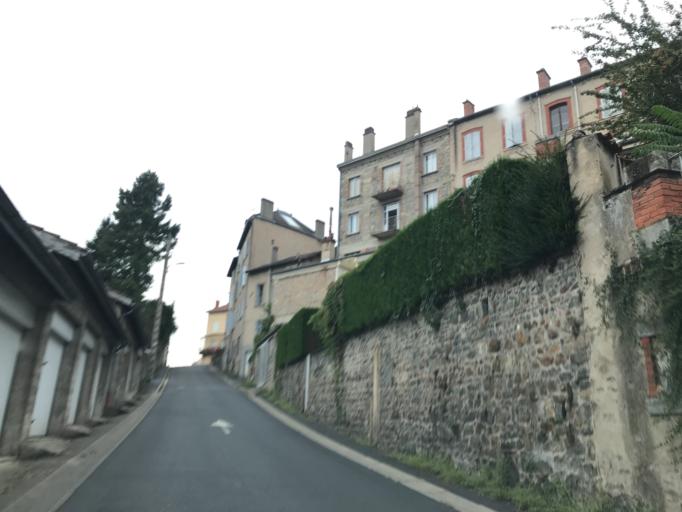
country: FR
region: Auvergne
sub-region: Departement du Puy-de-Dome
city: Thiers
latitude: 45.8592
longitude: 3.5446
